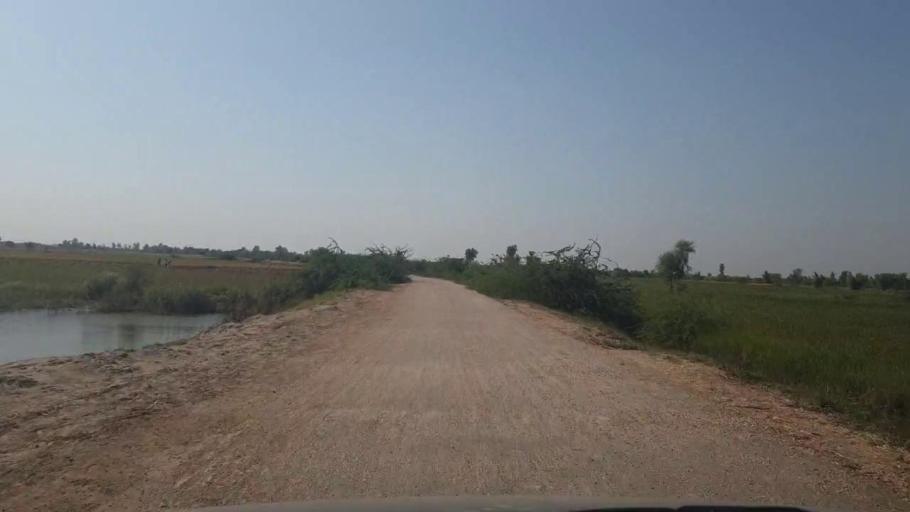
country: PK
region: Sindh
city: Badin
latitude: 24.5574
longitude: 68.8445
